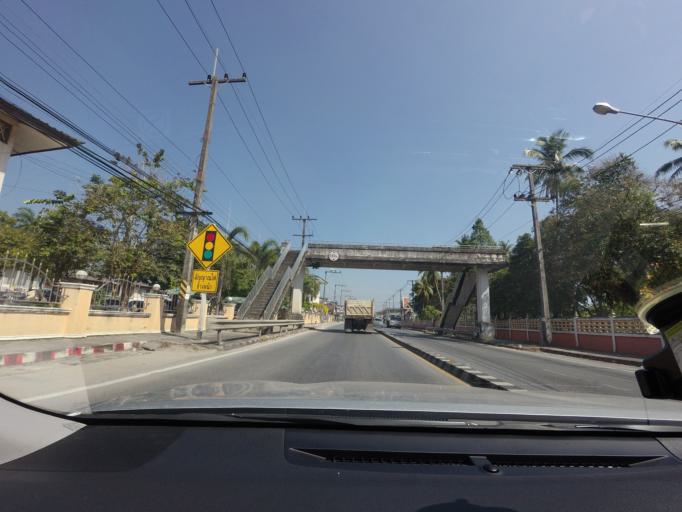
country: TH
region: Nakhon Si Thammarat
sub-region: Amphoe Nopphitam
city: Nopphitam
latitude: 8.9042
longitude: 99.9002
